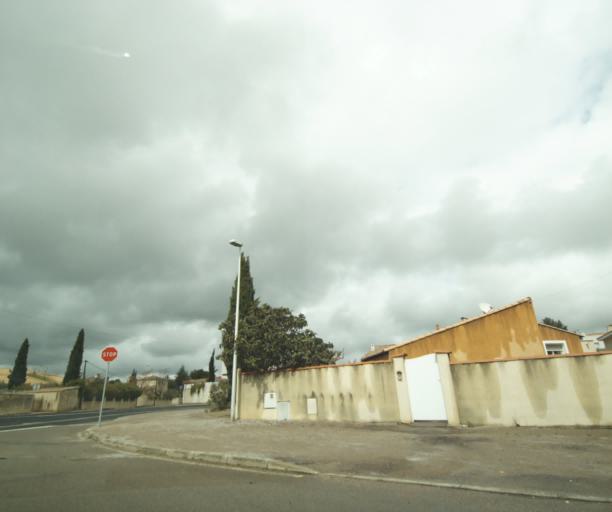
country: FR
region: Languedoc-Roussillon
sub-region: Departement de l'Herault
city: Cournonsec
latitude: 43.5526
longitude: 3.7101
